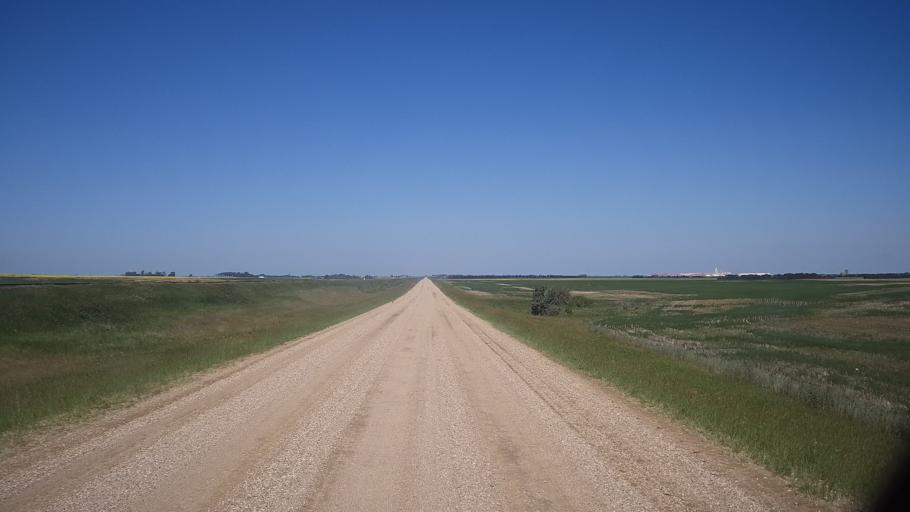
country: CA
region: Saskatchewan
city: Watrous
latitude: 51.8678
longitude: -105.9843
